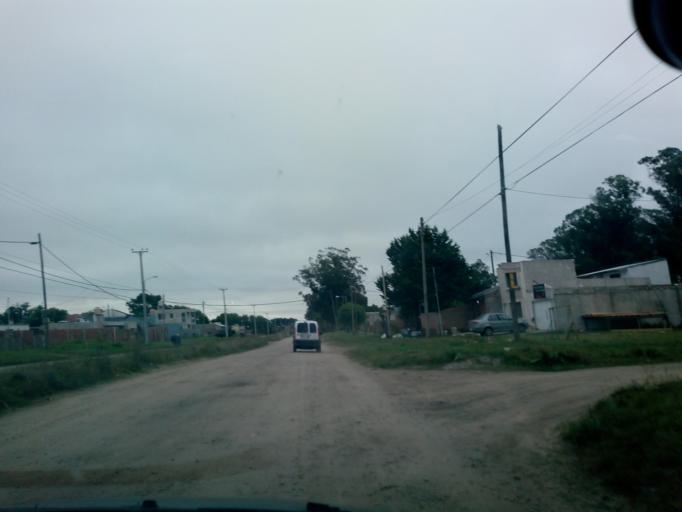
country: AR
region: Buenos Aires
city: Mar del Plata
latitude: -38.0661
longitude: -57.5679
